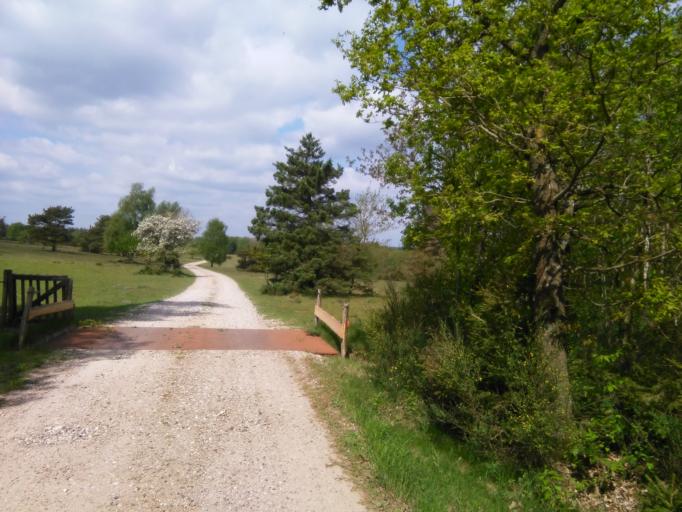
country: DK
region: Central Jutland
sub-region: Silkeborg Kommune
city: Svejbaek
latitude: 56.0581
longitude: 9.6510
